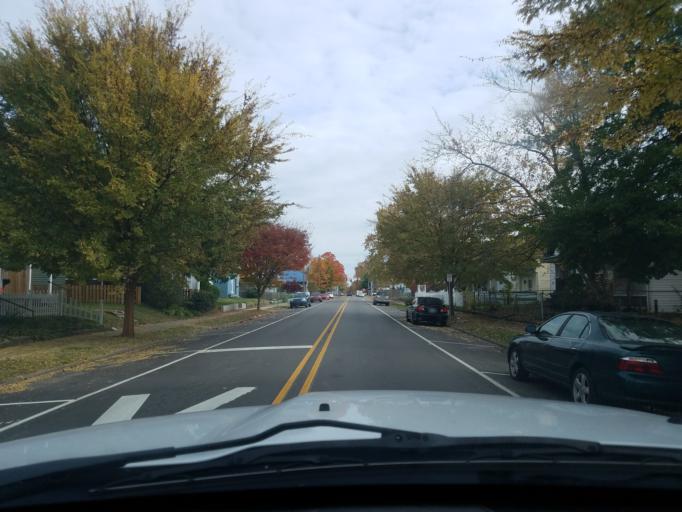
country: US
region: Indiana
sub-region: Floyd County
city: New Albany
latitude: 38.2926
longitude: -85.8098
